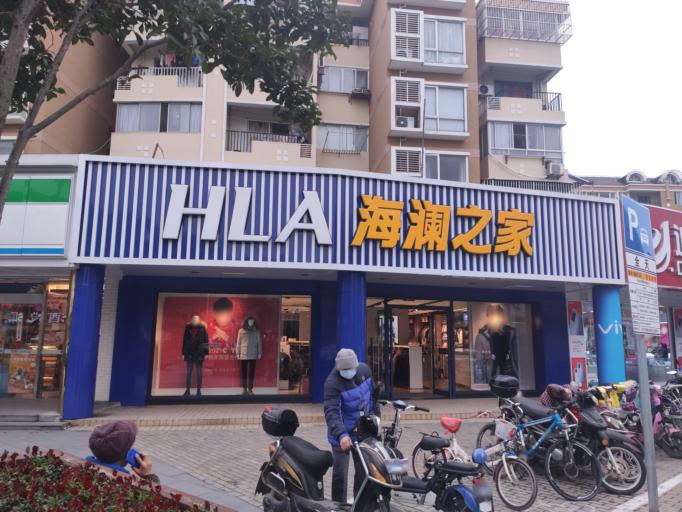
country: CN
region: Shanghai Shi
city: Huacao
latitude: 31.2082
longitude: 121.2923
